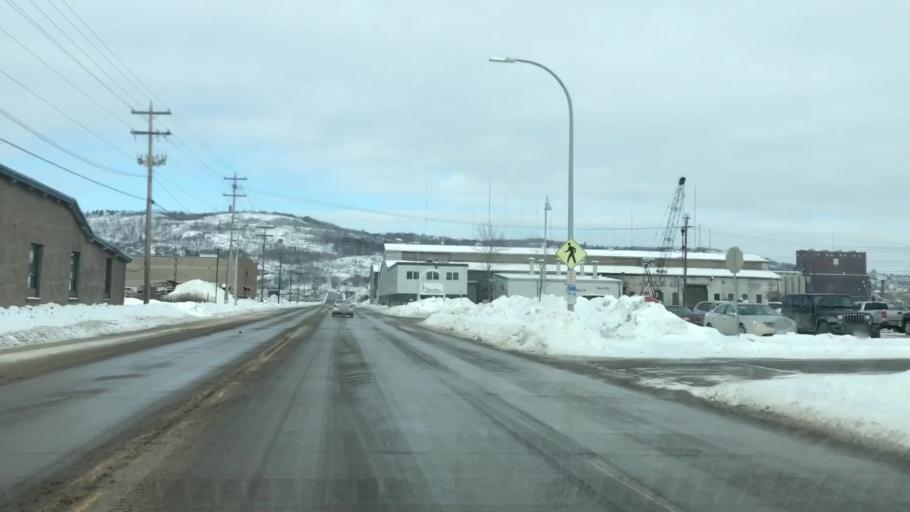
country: US
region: Minnesota
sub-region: Saint Louis County
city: Duluth
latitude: 46.7629
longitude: -92.1116
